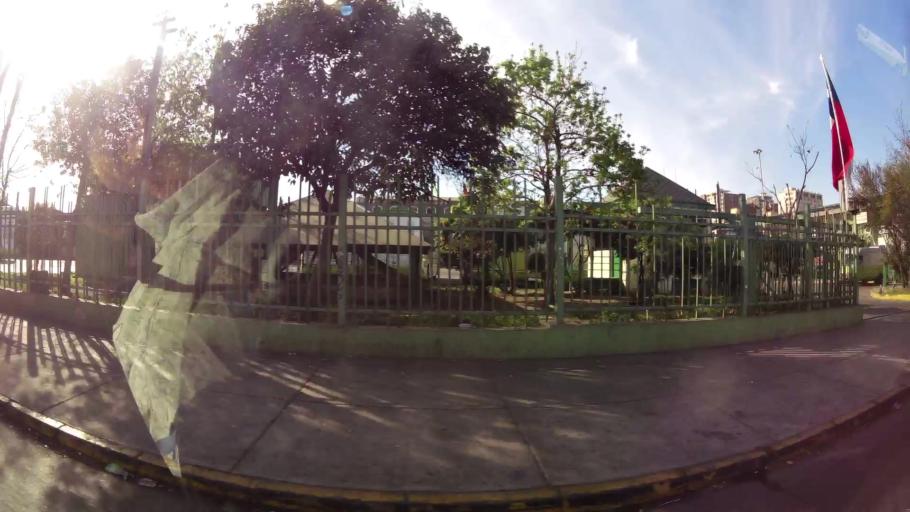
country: CL
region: Santiago Metropolitan
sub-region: Provincia de Santiago
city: Santiago
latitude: -33.4543
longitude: -70.6864
